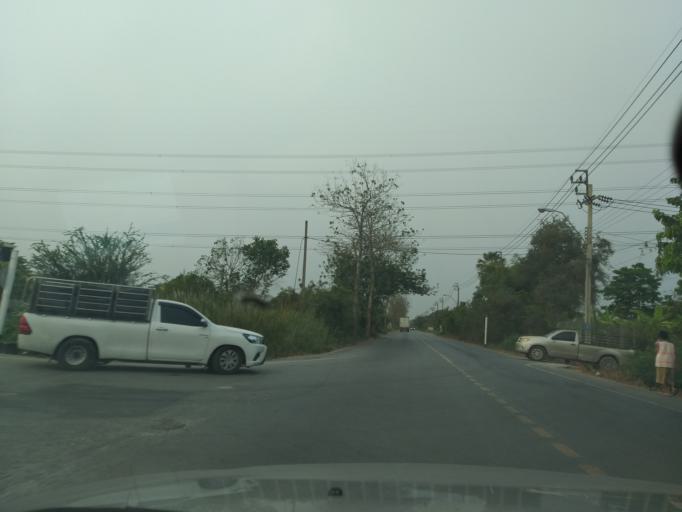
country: TH
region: Bangkok
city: Nong Chok
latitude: 13.9284
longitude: 100.8929
